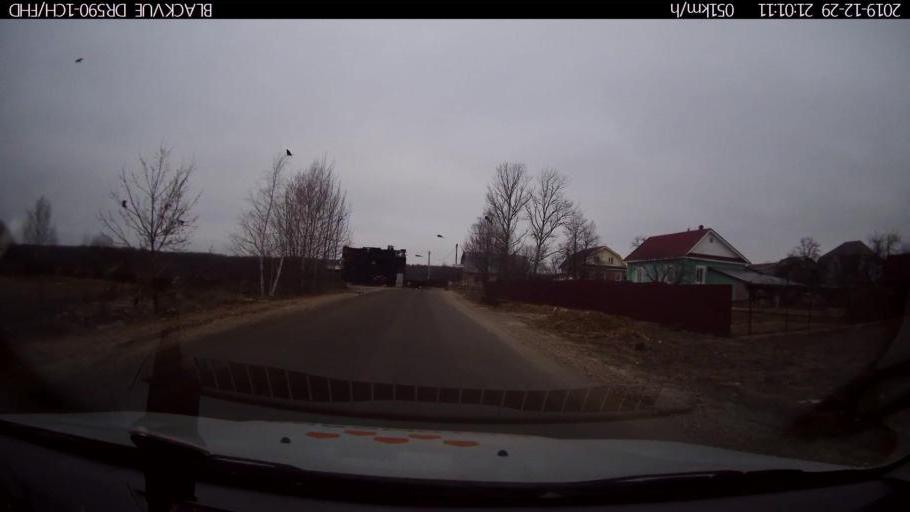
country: RU
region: Nizjnij Novgorod
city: Afonino
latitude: 56.1871
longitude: 43.9898
